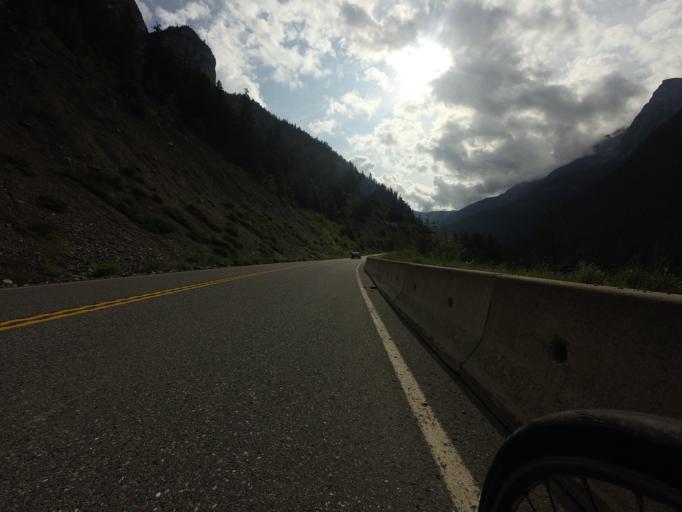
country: CA
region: British Columbia
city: Lillooet
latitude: 50.6422
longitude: -122.0489
